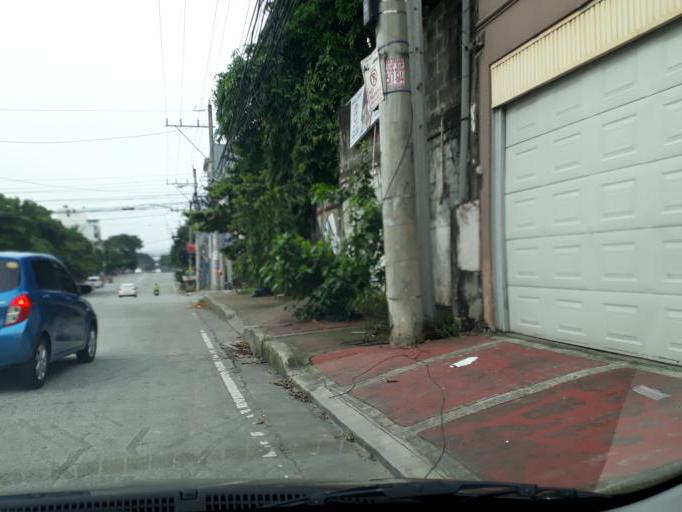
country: PH
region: Calabarzon
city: Del Monte
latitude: 14.6329
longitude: 121.0304
